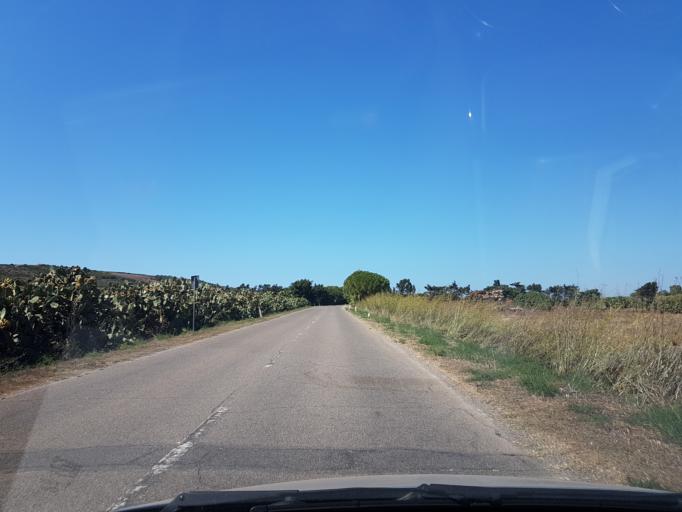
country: IT
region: Sardinia
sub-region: Provincia di Oristano
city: Cabras
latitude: 39.9417
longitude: 8.4575
